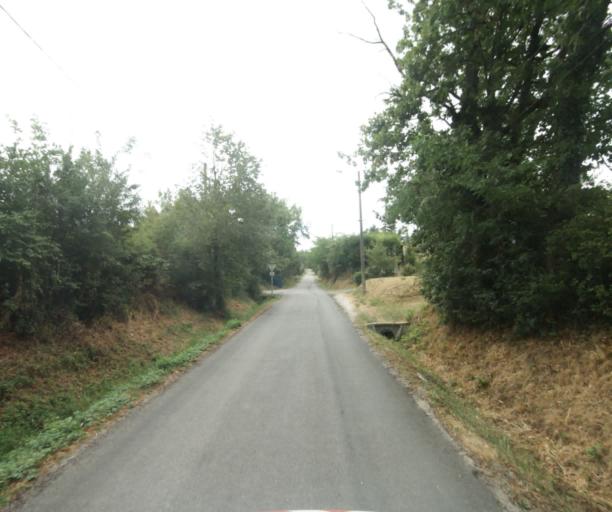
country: FR
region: Midi-Pyrenees
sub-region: Departement de la Haute-Garonne
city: Revel
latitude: 43.4493
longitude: 1.9980
